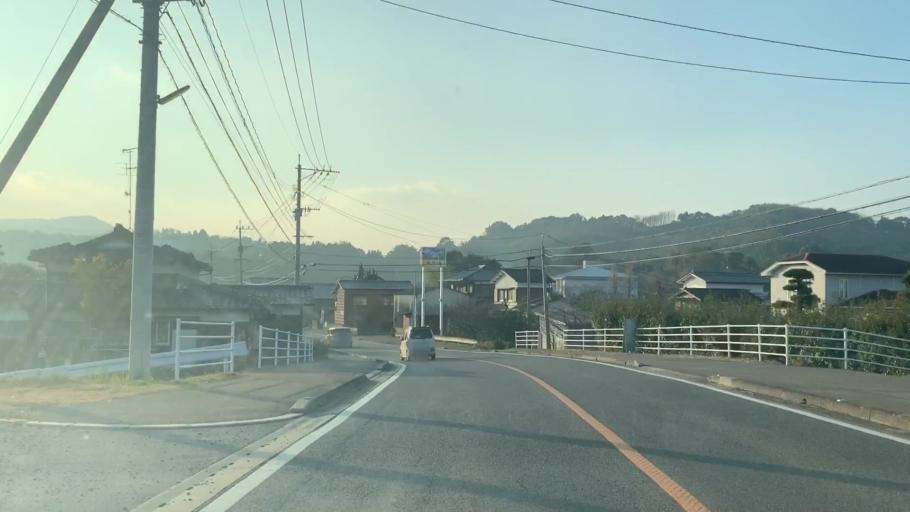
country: JP
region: Saga Prefecture
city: Saga-shi
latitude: 33.2721
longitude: 130.1863
